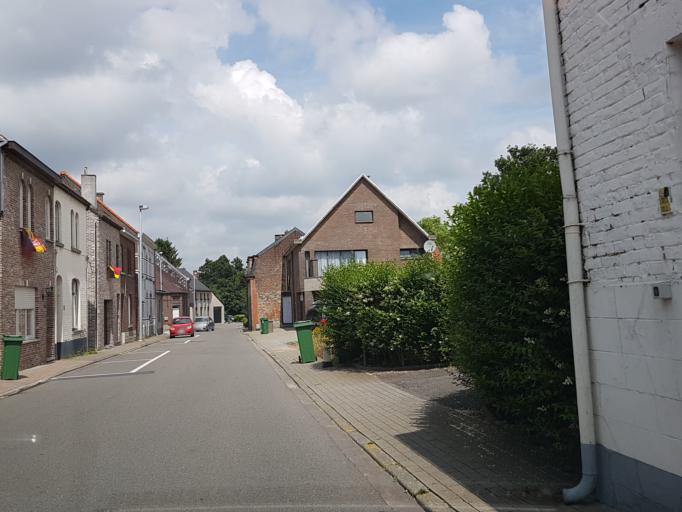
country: BE
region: Flanders
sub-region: Provincie Oost-Vlaanderen
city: Denderleeuw
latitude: 50.9116
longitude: 4.1056
